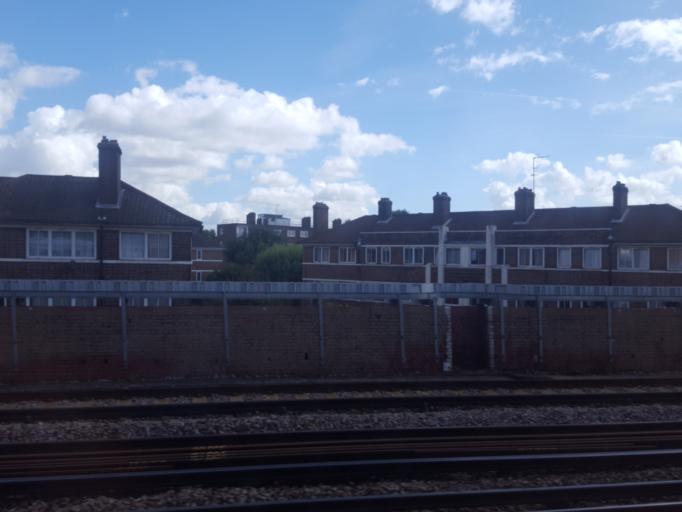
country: GB
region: England
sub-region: Greater London
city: City of London
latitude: 51.4986
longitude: -0.0735
